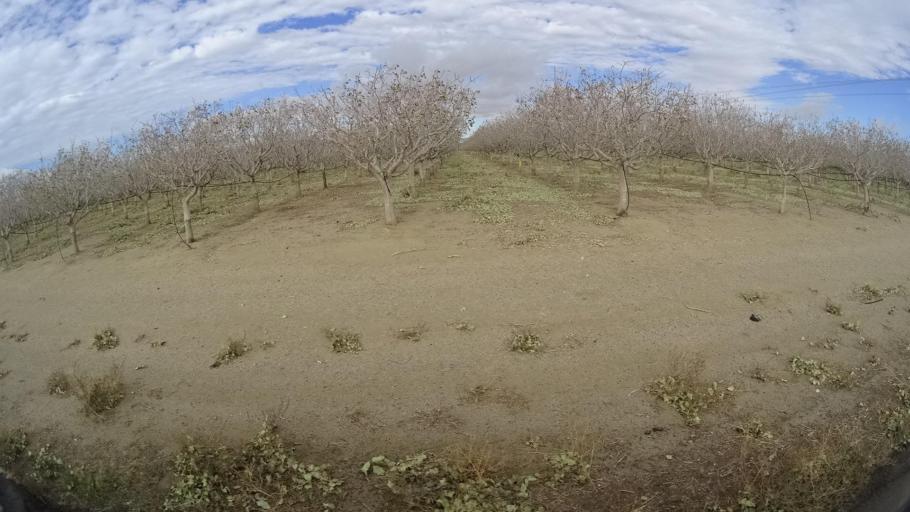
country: US
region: California
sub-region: Kern County
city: Rosamond
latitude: 34.8199
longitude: -118.3202
